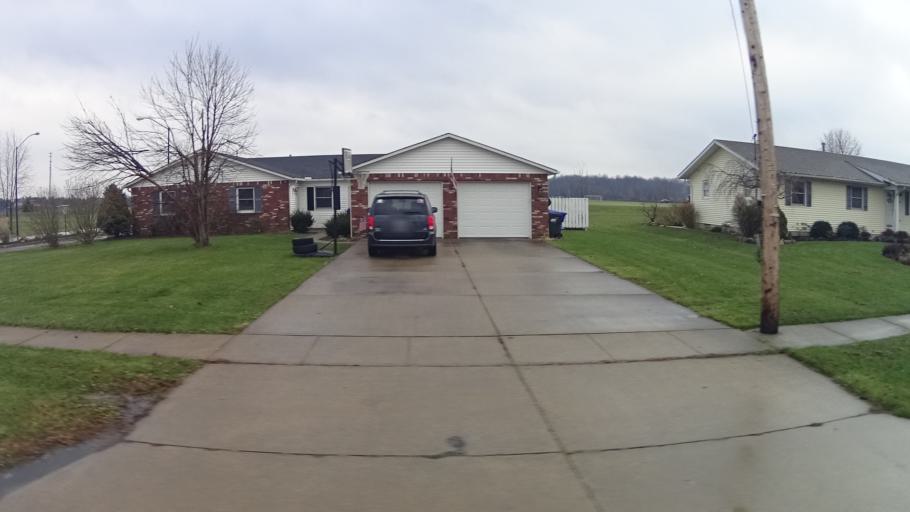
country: US
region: Ohio
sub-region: Lorain County
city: Lagrange
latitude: 41.2373
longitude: -82.1281
